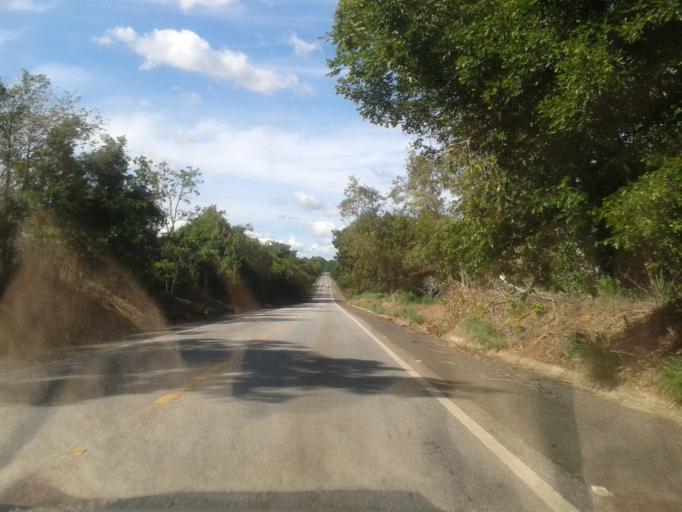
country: BR
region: Goias
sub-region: Mozarlandia
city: Mozarlandia
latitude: -14.9650
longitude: -50.5797
